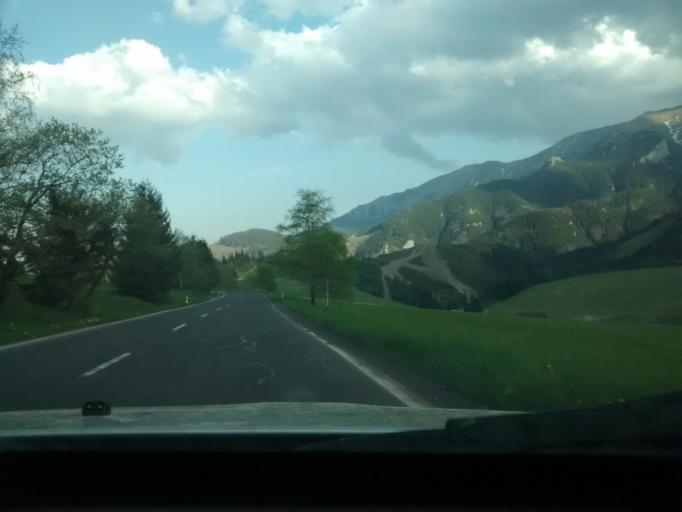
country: SK
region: Presovsky
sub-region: Okres Poprad
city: Zdiar
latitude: 49.2771
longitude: 20.2209
